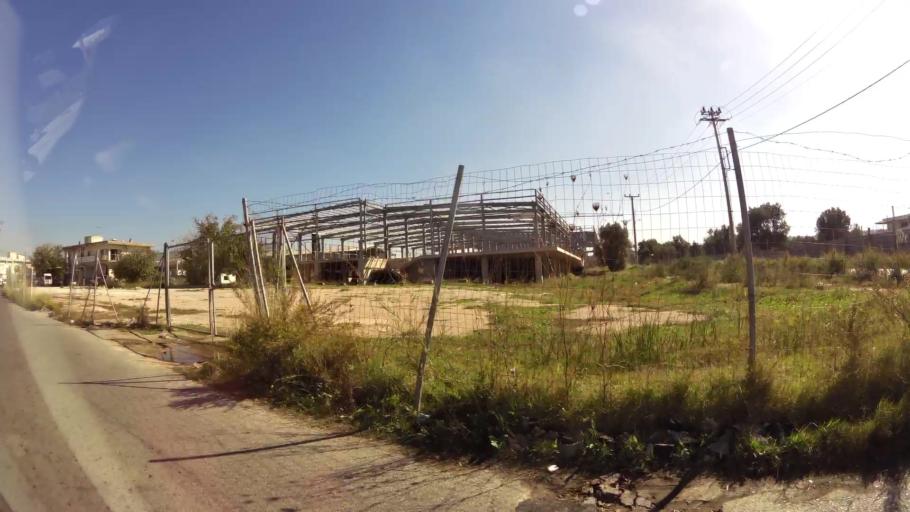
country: GR
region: Attica
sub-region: Nomarchia Athinas
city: Lykovrysi
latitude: 38.0751
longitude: 23.7783
